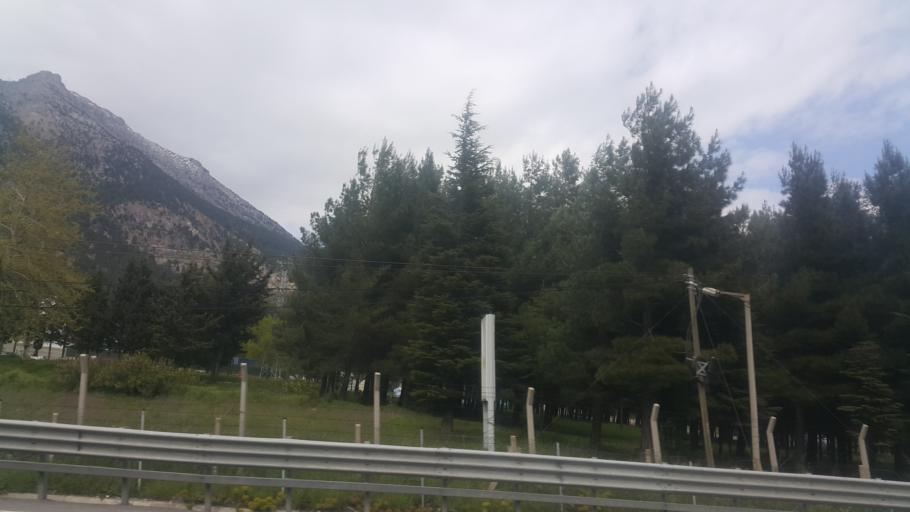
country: TR
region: Adana
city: Pozanti
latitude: 37.4648
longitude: 34.8717
